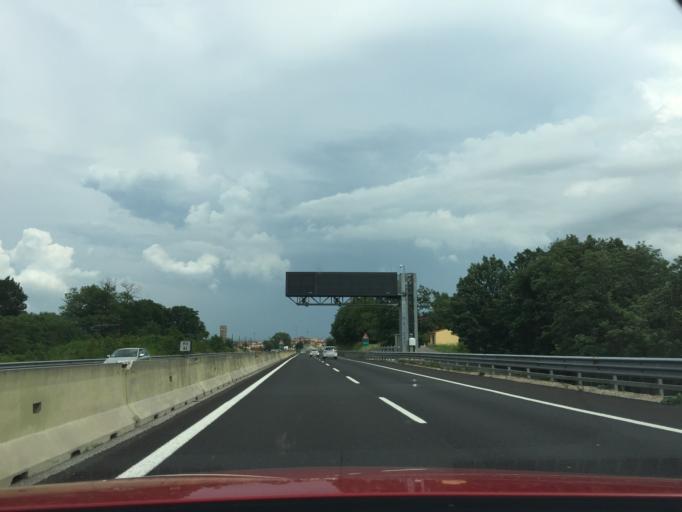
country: IT
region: Tuscany
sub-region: Provincia di Lucca
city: Altopascio
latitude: 43.8150
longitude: 10.6624
